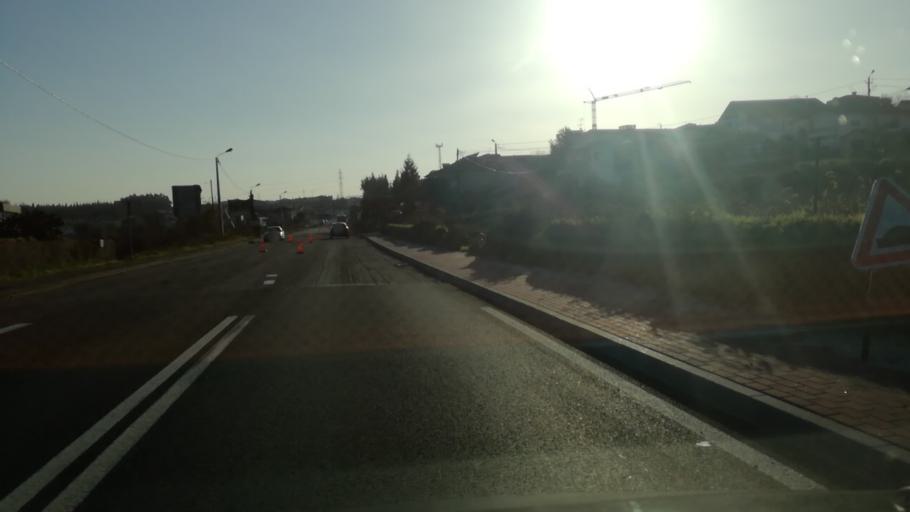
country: PT
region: Braga
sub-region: Vila Nova de Famalicao
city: Ferreiros
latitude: 41.3608
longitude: -8.5481
